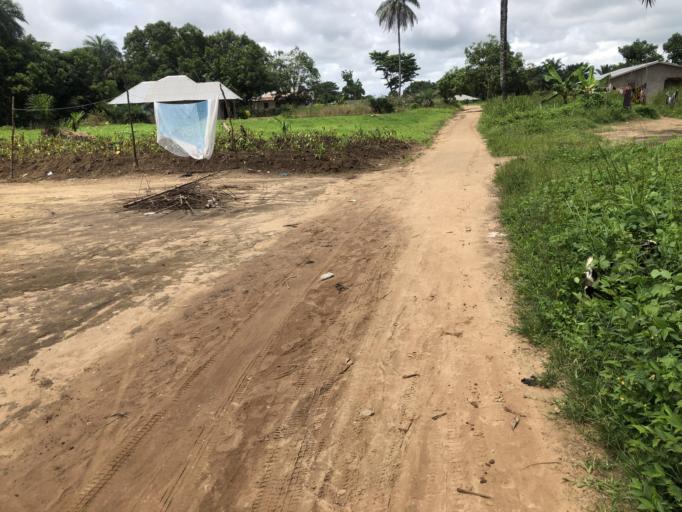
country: SL
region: Northern Province
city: Lunsar
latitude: 8.7154
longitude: -12.5173
